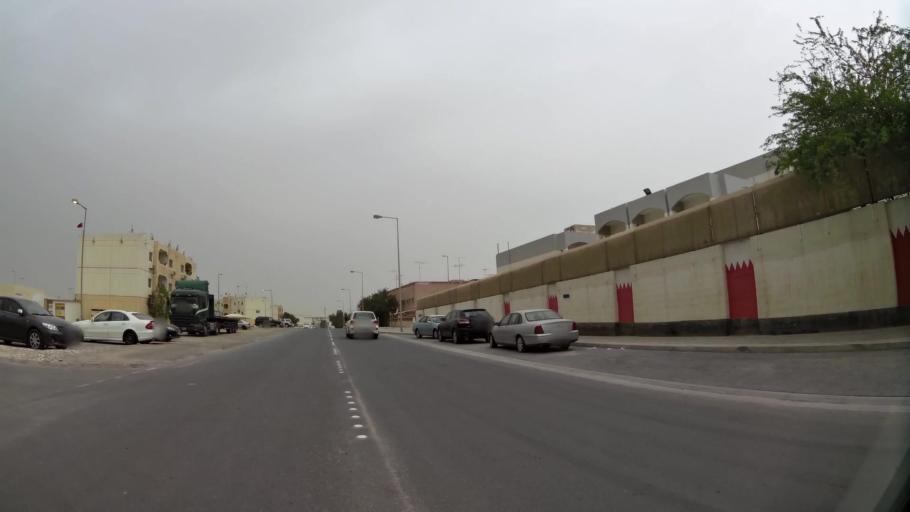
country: BH
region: Northern
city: Madinat `Isa
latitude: 26.1750
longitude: 50.5422
